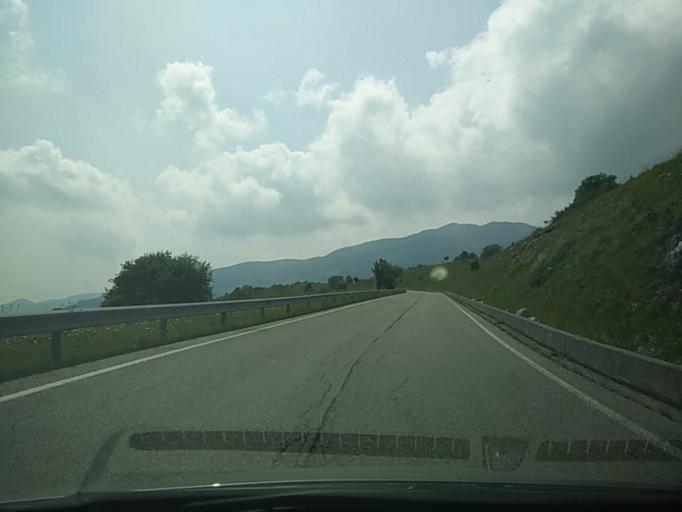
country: IT
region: Friuli Venezia Giulia
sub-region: Provincia di Pordenone
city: Budoia
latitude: 46.0807
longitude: 12.5255
